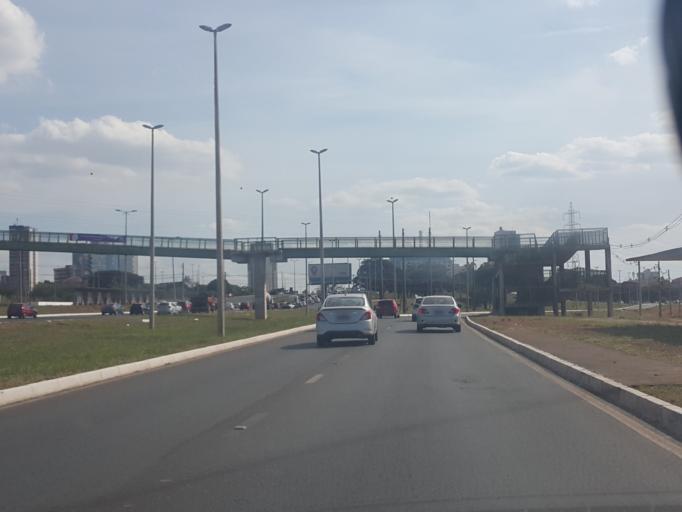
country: BR
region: Federal District
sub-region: Brasilia
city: Brasilia
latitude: -15.8308
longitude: -48.0458
